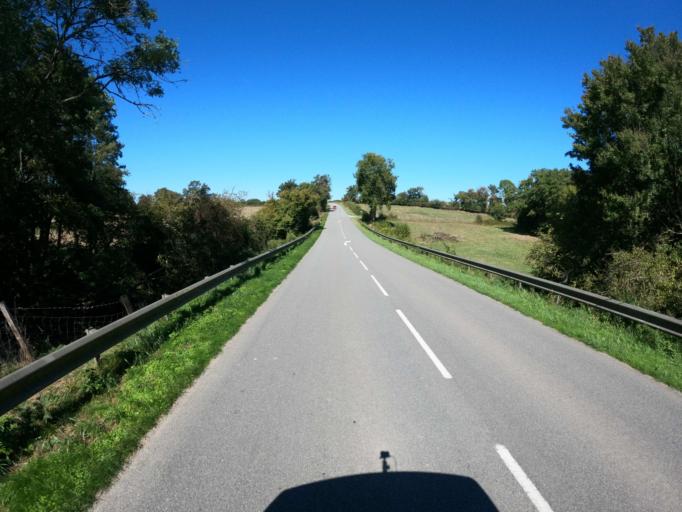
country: FR
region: Limousin
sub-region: Departement de la Haute-Vienne
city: Le Dorat
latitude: 46.2556
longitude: 1.0417
